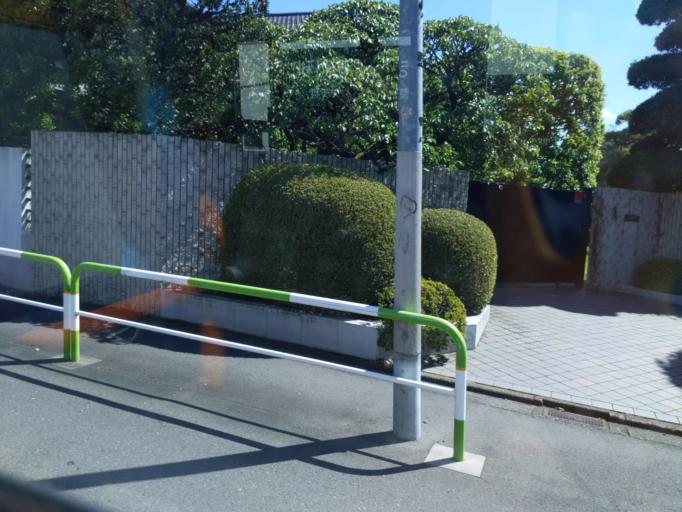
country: JP
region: Tokyo
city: Chofugaoka
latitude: 35.6462
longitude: 139.5923
